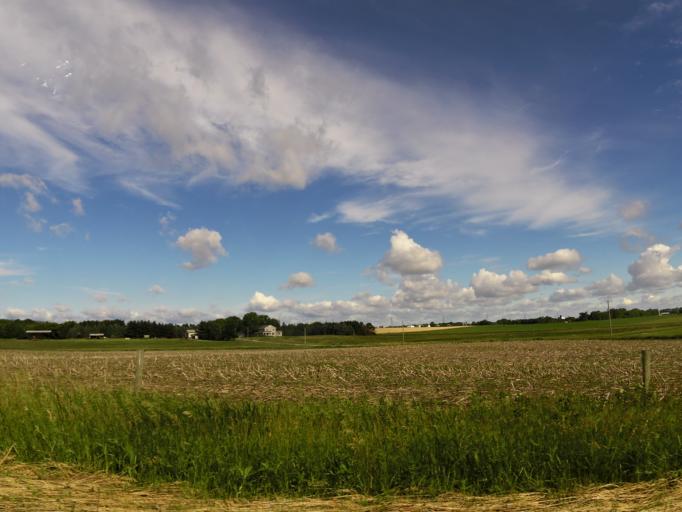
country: US
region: Minnesota
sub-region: Goodhue County
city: Cannon Falls
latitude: 44.6144
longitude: -92.9754
